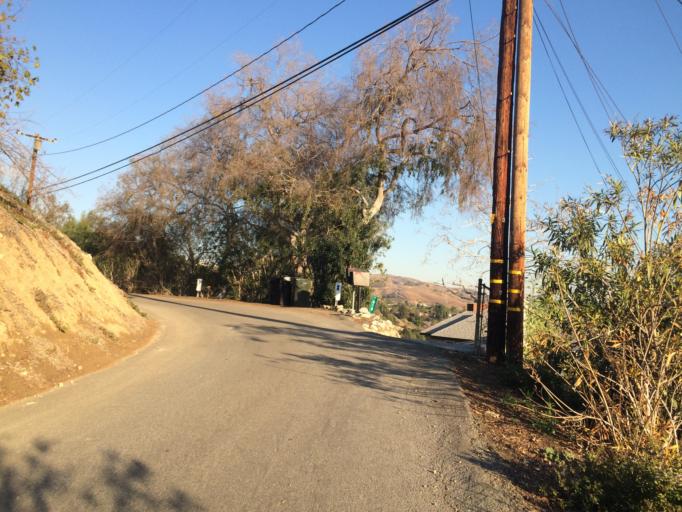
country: US
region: California
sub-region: Los Angeles County
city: La Habra Heights
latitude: 33.9534
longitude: -117.9446
